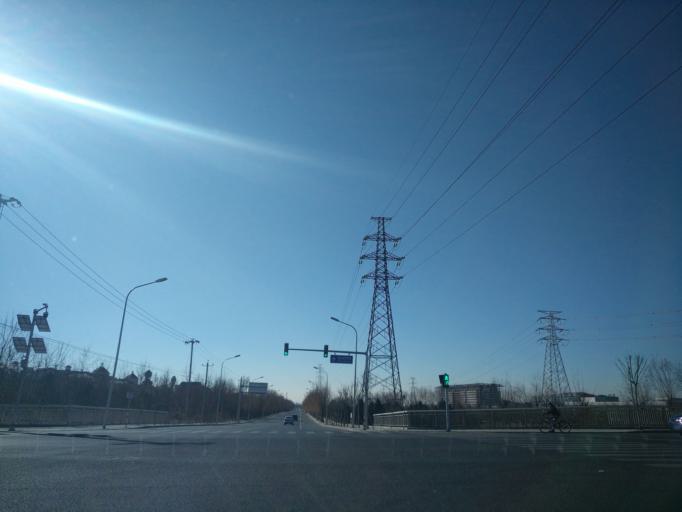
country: CN
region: Beijing
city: Qingyundian
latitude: 39.7523
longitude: 116.5312
